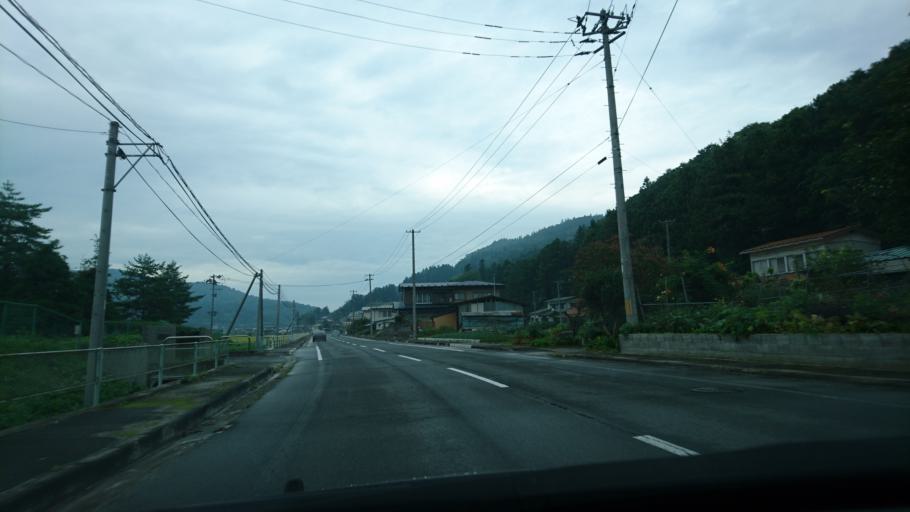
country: JP
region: Iwate
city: Ichinoseki
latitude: 38.9694
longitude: 141.2447
